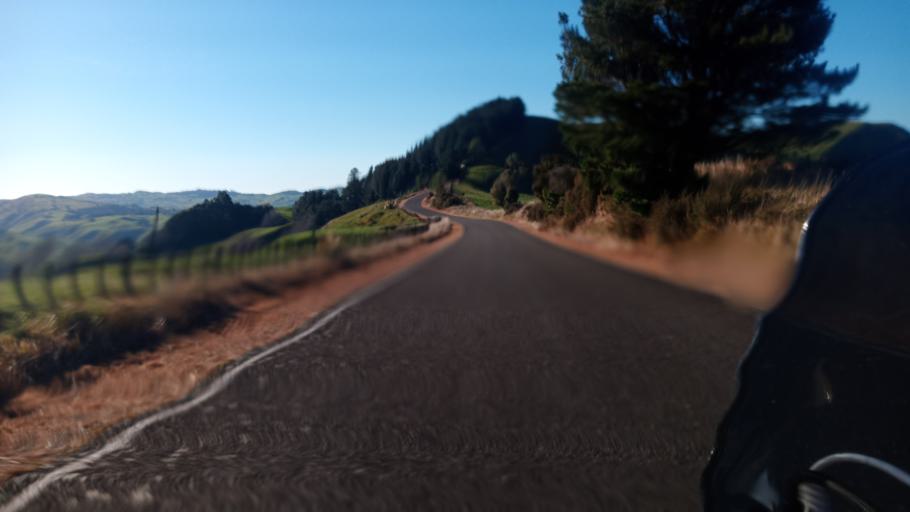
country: NZ
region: Hawke's Bay
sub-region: Wairoa District
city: Wairoa
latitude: -38.8314
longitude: 177.2814
